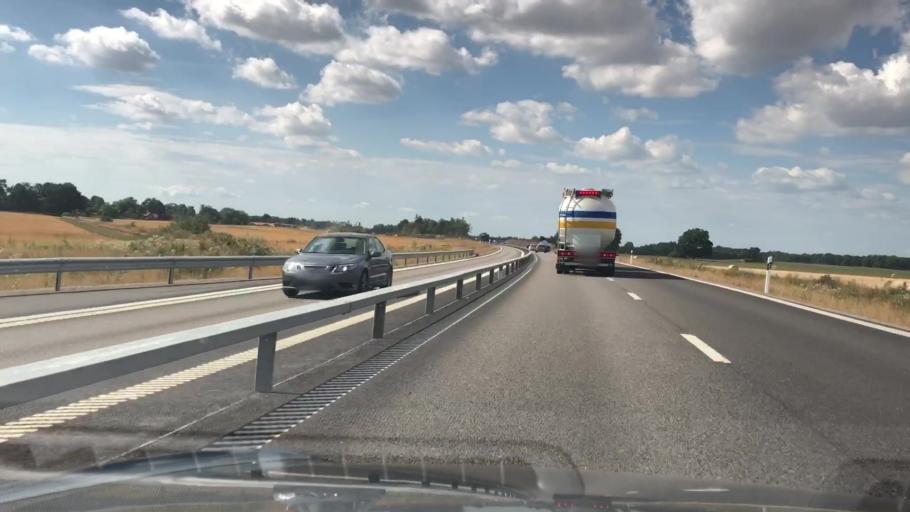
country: SE
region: Kalmar
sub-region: Kalmar Kommun
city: Rinkabyholm
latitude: 56.6613
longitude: 16.2561
